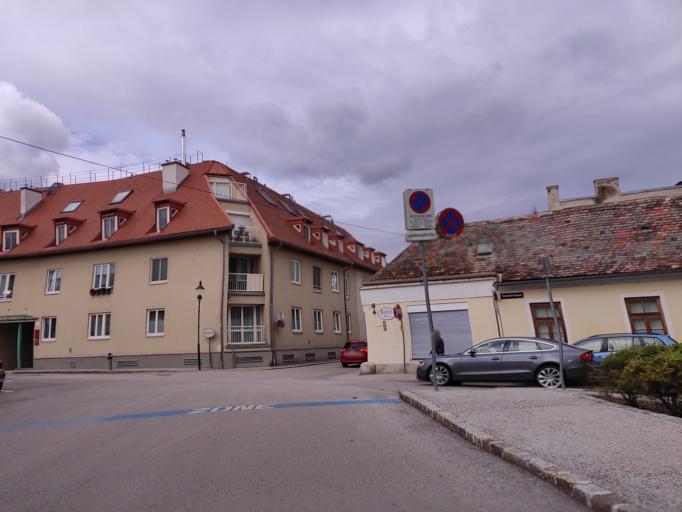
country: AT
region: Lower Austria
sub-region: Politischer Bezirk Baden
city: Baden
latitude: 48.0070
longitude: 16.2382
